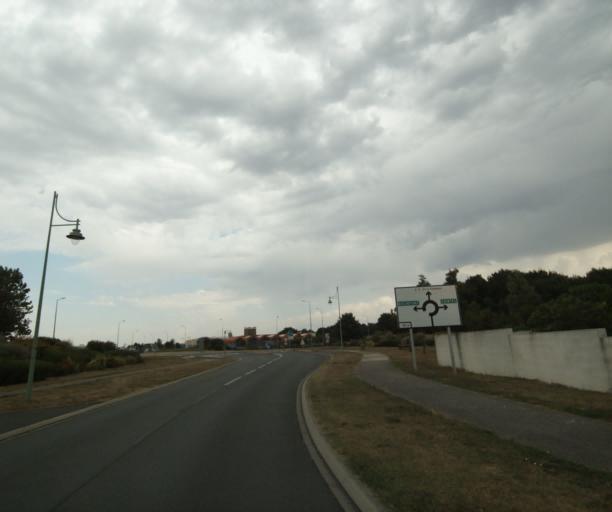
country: FR
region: Poitou-Charentes
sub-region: Departement de la Charente-Maritime
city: Tonnay-Charente
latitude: 45.9495
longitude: -0.8961
